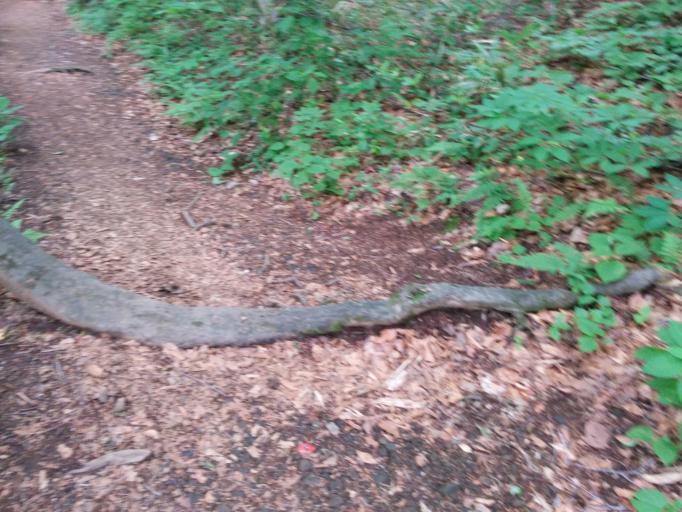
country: JP
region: Aomori
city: Hirosaki
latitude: 40.5197
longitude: 140.1703
